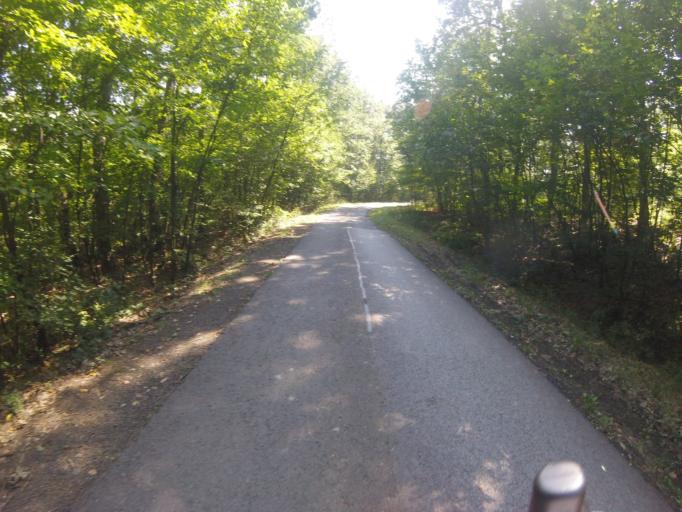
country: HU
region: Nograd
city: Bujak
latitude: 47.9026
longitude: 19.5150
